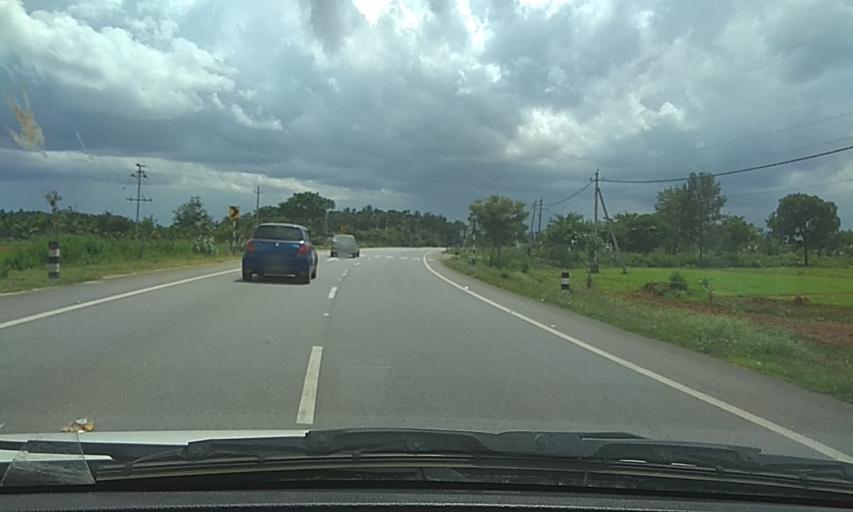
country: IN
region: Karnataka
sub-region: Tumkur
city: Tumkur
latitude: 13.2319
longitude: 77.0704
